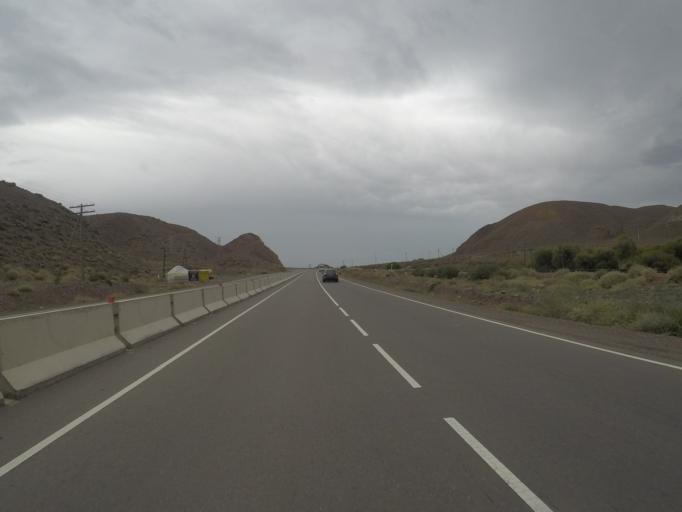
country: KG
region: Ysyk-Koel
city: Balykchy
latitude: 42.4629
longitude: 76.0082
